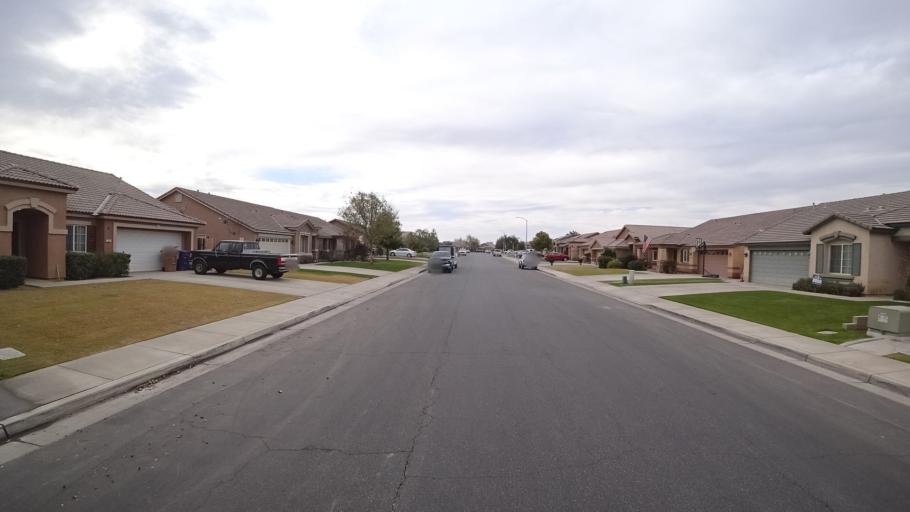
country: US
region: California
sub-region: Kern County
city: Rosedale
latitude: 35.4094
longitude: -119.1477
